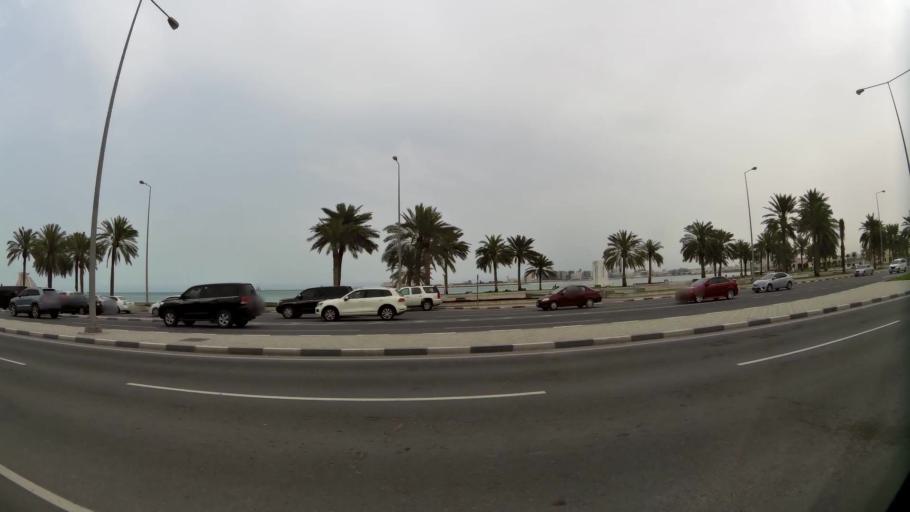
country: QA
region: Baladiyat ad Dawhah
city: Doha
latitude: 25.3097
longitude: 51.5188
